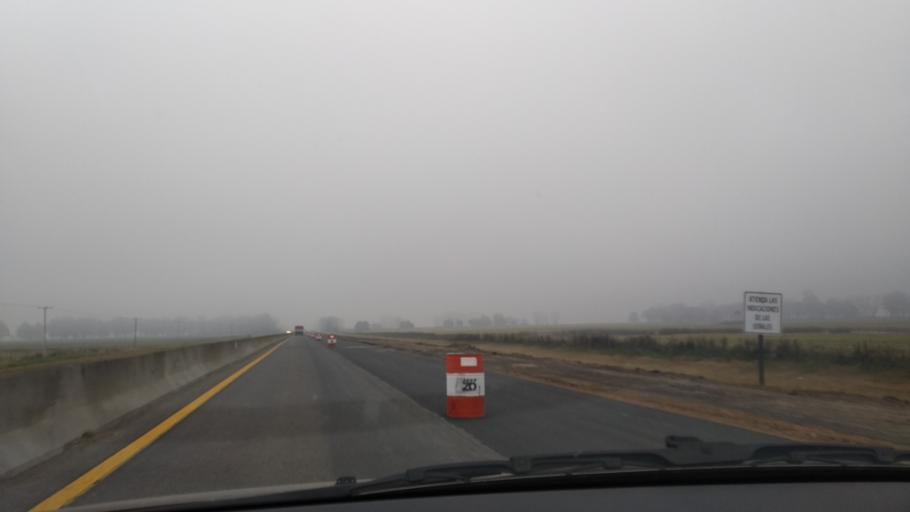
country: AR
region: Buenos Aires
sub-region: Partido de Azul
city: Azul
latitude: -36.8472
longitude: -59.9481
